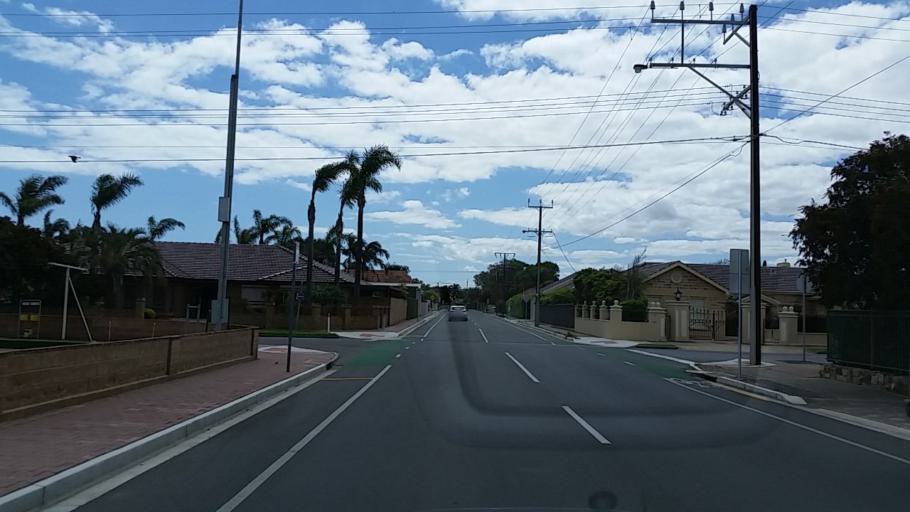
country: AU
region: South Australia
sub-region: Holdfast Bay
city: North Brighton
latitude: -34.9996
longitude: 138.5172
